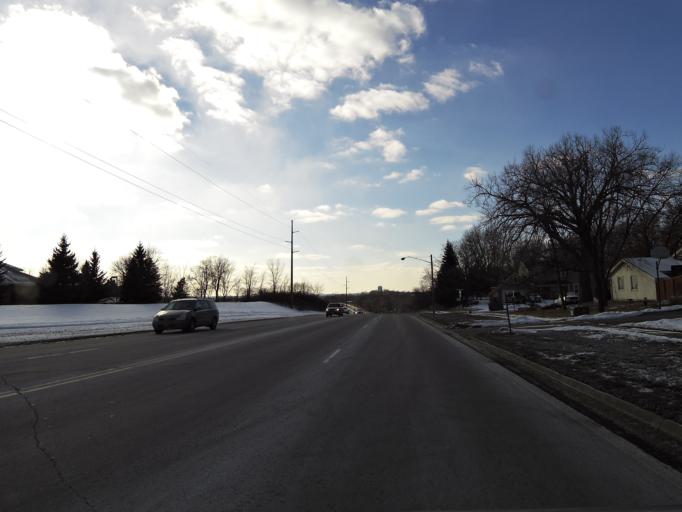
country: US
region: Minnesota
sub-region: Dakota County
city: Burnsville
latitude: 44.7537
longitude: -93.2718
